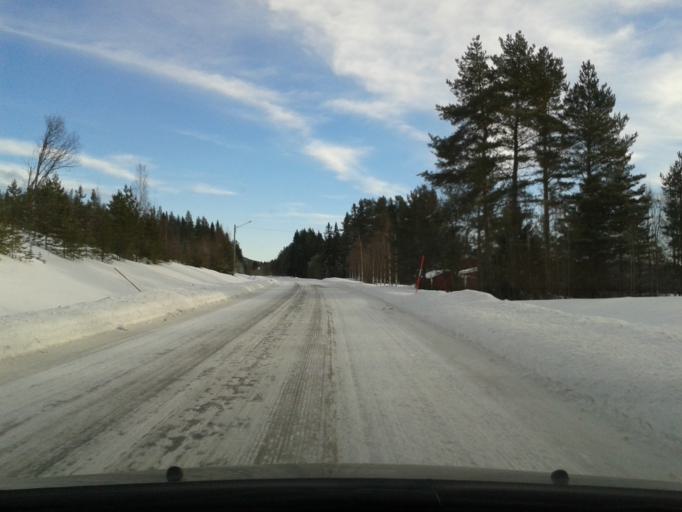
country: SE
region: Vaesterbotten
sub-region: Asele Kommun
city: Asele
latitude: 64.3450
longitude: 17.0033
